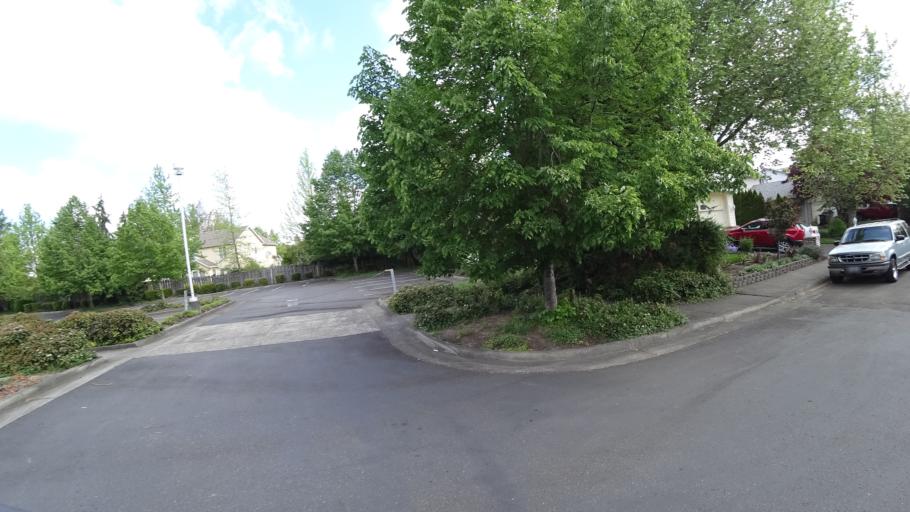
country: US
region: Oregon
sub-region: Washington County
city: Aloha
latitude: 45.5137
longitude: -122.8865
